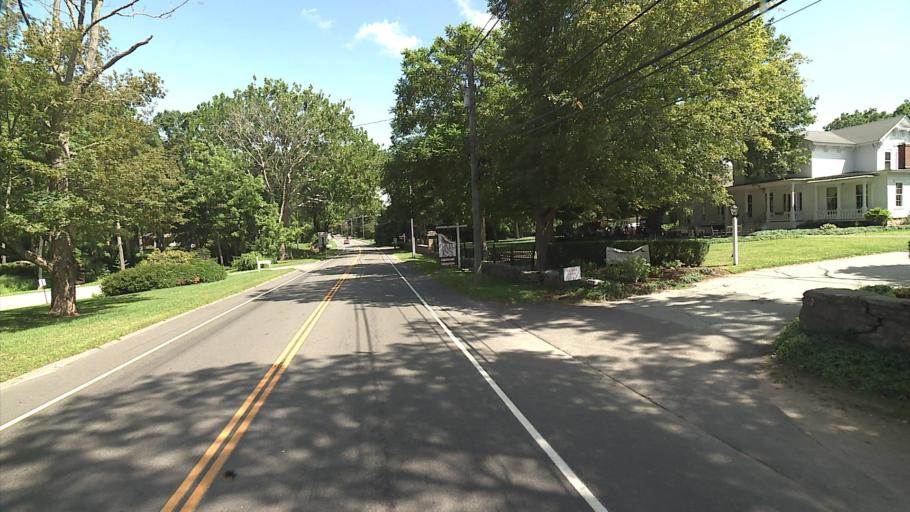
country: US
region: Connecticut
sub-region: Middlesex County
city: Old Saybrook Center
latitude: 41.3245
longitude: -72.3270
